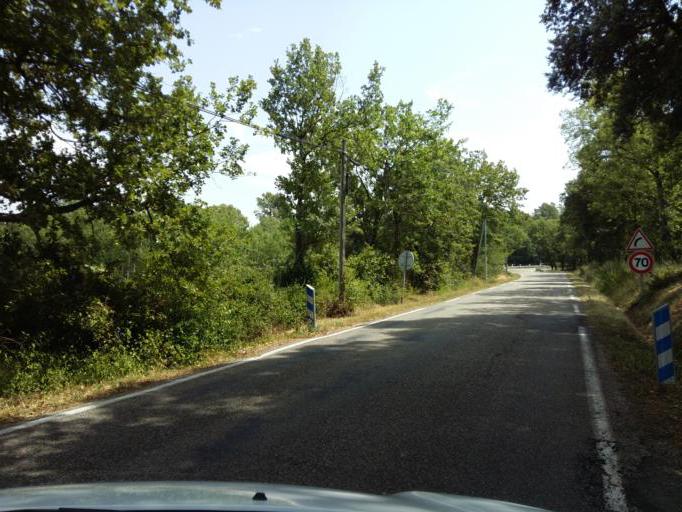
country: FR
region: Provence-Alpes-Cote d'Azur
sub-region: Departement du Vaucluse
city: Bollene
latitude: 44.2676
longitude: 4.7879
